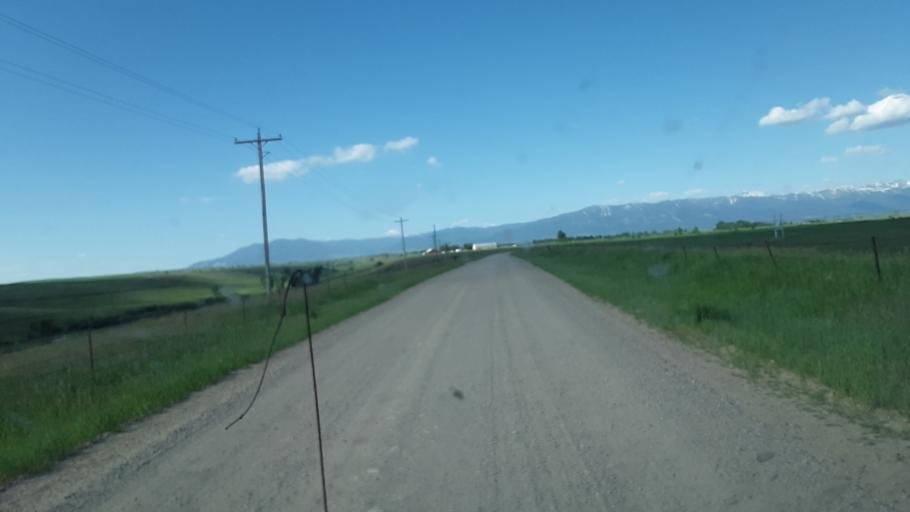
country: US
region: Montana
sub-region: Carbon County
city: Red Lodge
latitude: 45.3431
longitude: -109.1578
